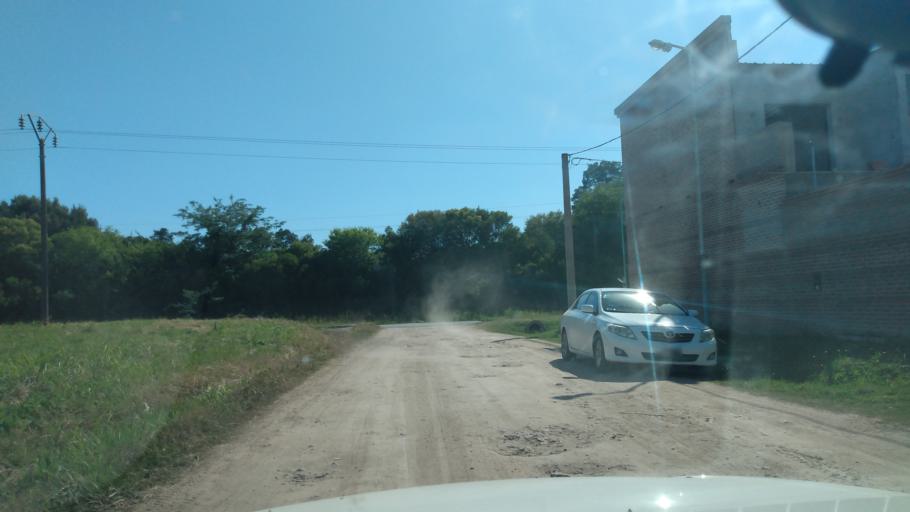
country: AR
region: Buenos Aires
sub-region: Partido de Lujan
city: Lujan
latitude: -34.5525
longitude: -59.1347
